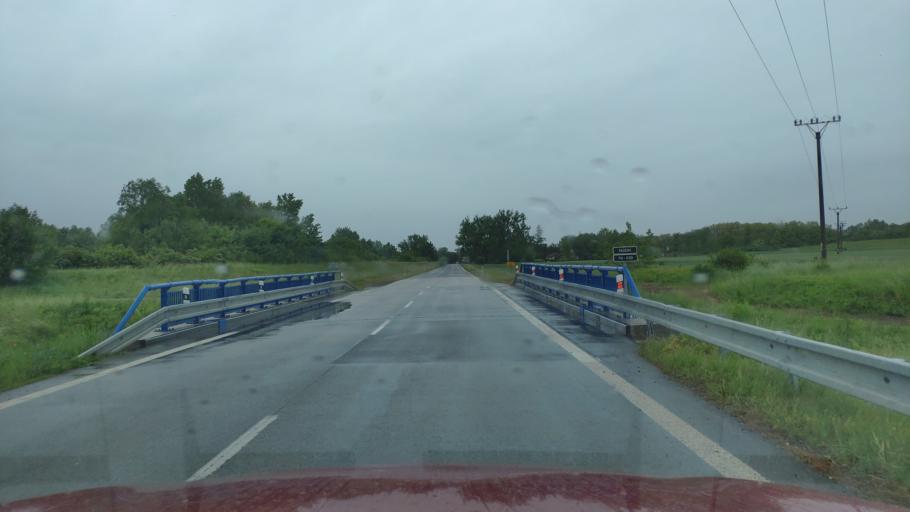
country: HU
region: Borsod-Abauj-Zemplen
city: Karcsa
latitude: 48.4326
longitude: 21.8538
